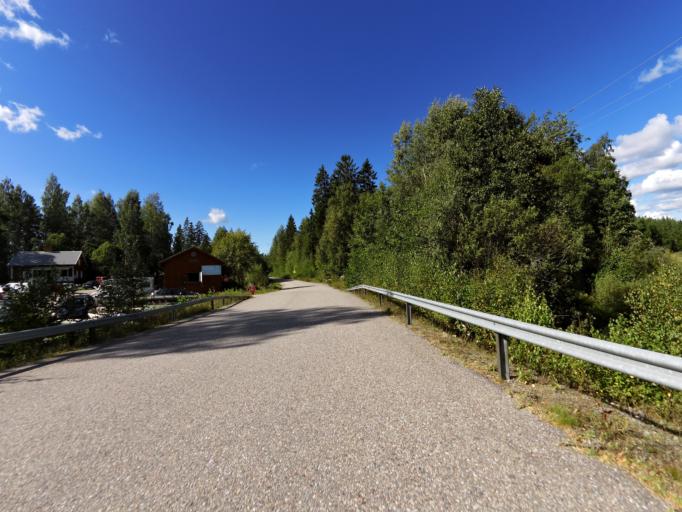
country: SE
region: Gaevleborg
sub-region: Gavle Kommun
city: Valbo
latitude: 60.7696
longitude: 16.9281
